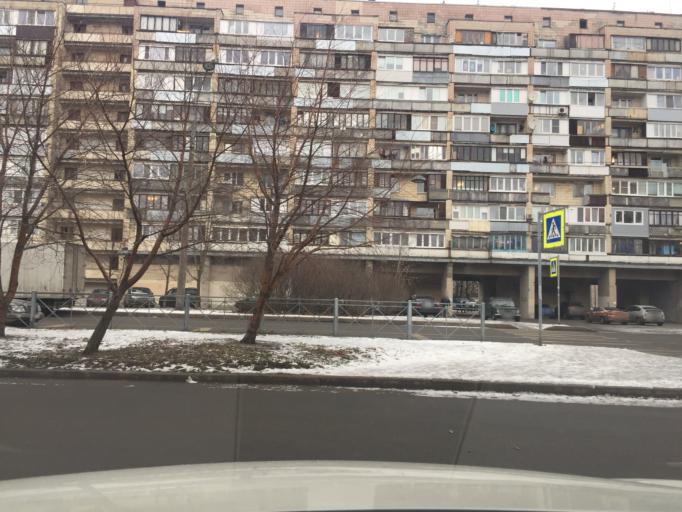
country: RU
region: St.-Petersburg
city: Vasyl'evsky Ostrov
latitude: 59.9433
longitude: 30.2344
